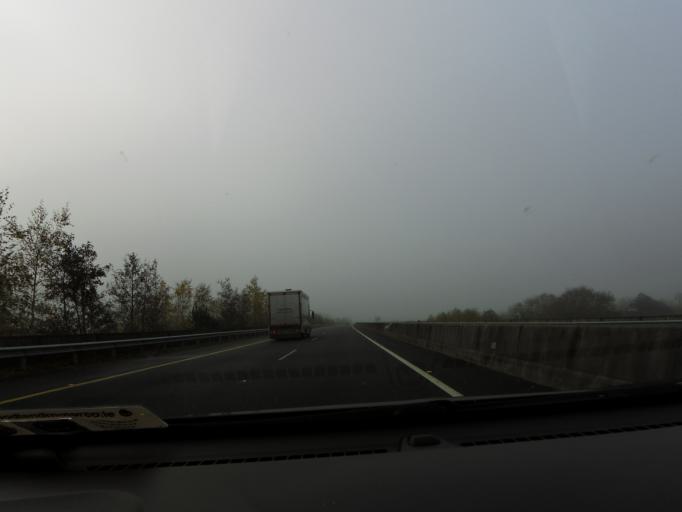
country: IE
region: Connaught
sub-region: County Galway
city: Ballinasloe
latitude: 53.3113
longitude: -8.2597
